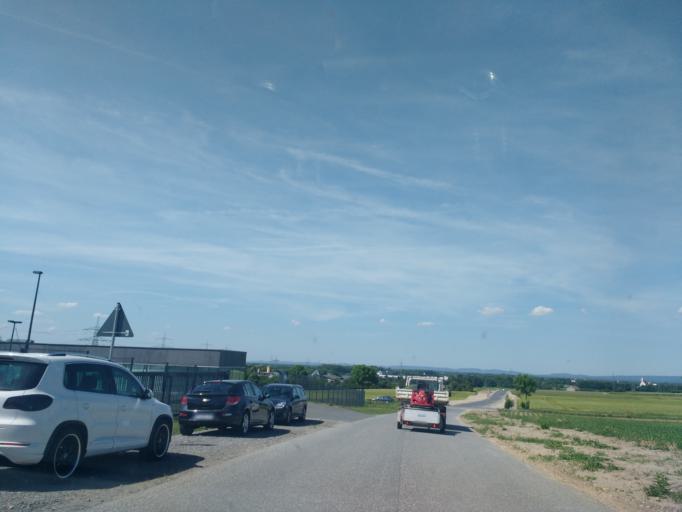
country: DE
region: North Rhine-Westphalia
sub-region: Regierungsbezirk Detmold
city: Paderborn
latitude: 51.6896
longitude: 8.7151
